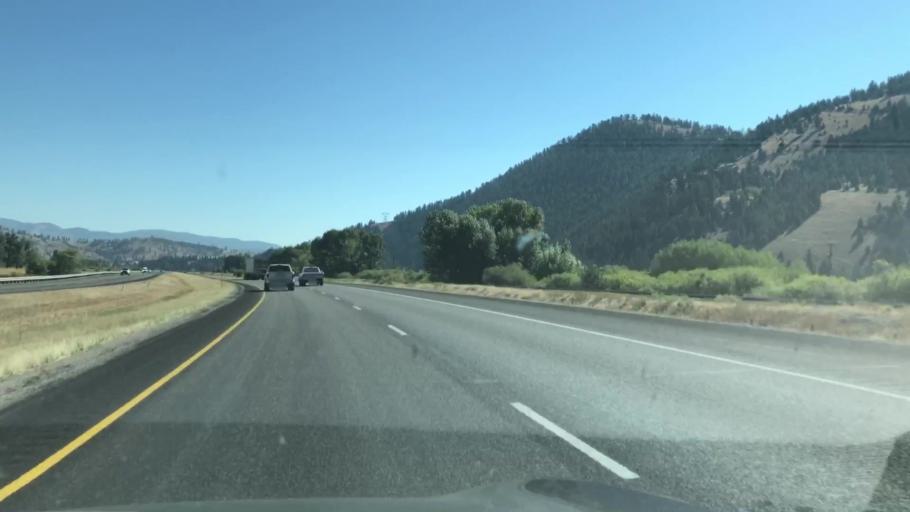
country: US
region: Montana
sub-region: Missoula County
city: Clinton
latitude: 46.6956
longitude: -113.4129
